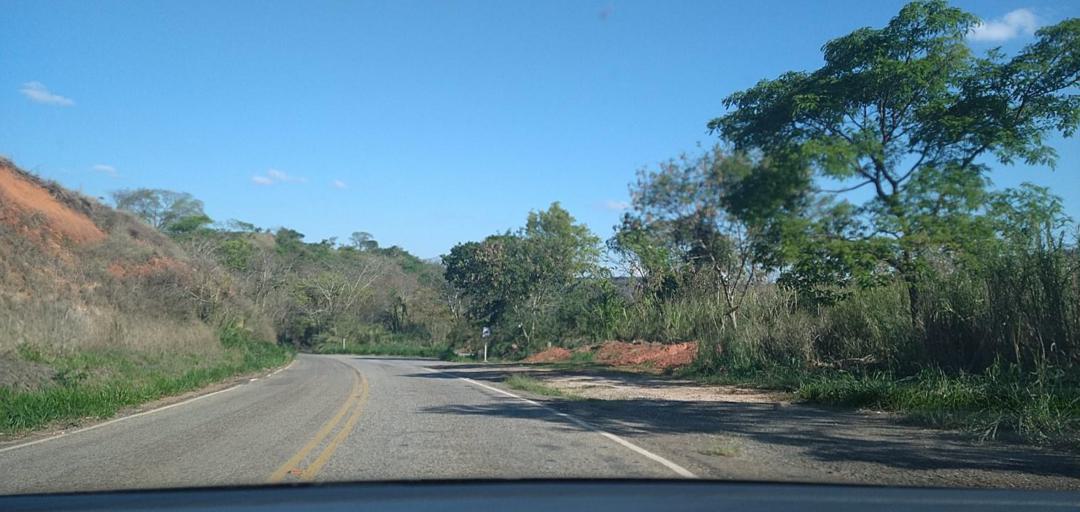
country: BR
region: Minas Gerais
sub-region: Ponte Nova
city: Ponte Nova
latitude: -20.2406
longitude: -42.8970
